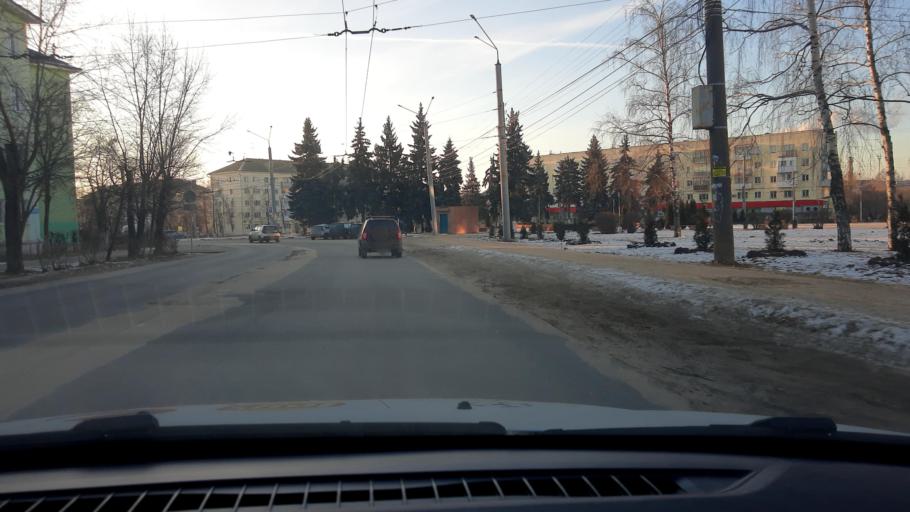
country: RU
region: Nizjnij Novgorod
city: Dzerzhinsk
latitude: 56.2455
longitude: 43.4557
